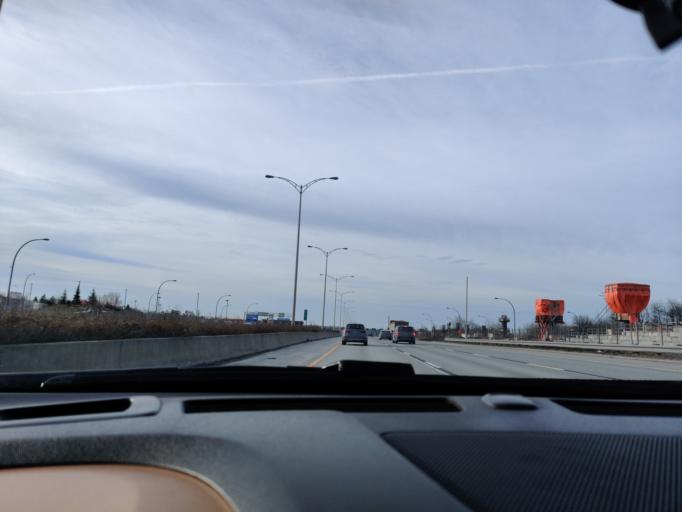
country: CA
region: Quebec
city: Kirkland
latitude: 45.4526
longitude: -73.8590
